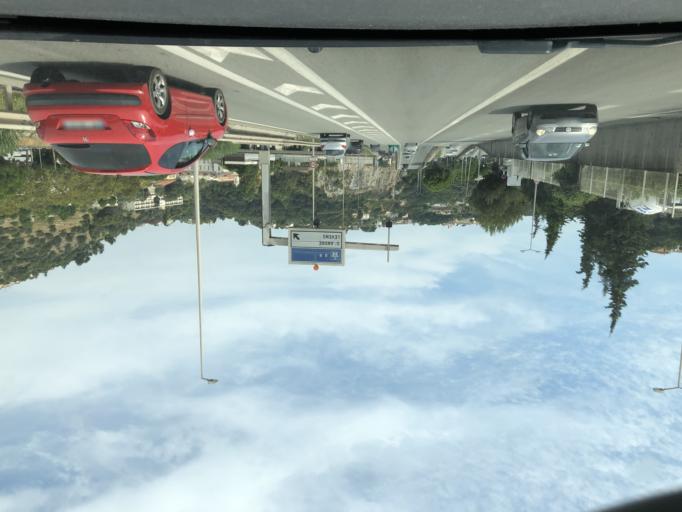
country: FR
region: Provence-Alpes-Cote d'Azur
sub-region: Departement des Alpes-Maritimes
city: Saint-Andre-de-la-Roche
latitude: 43.7324
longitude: 7.2893
